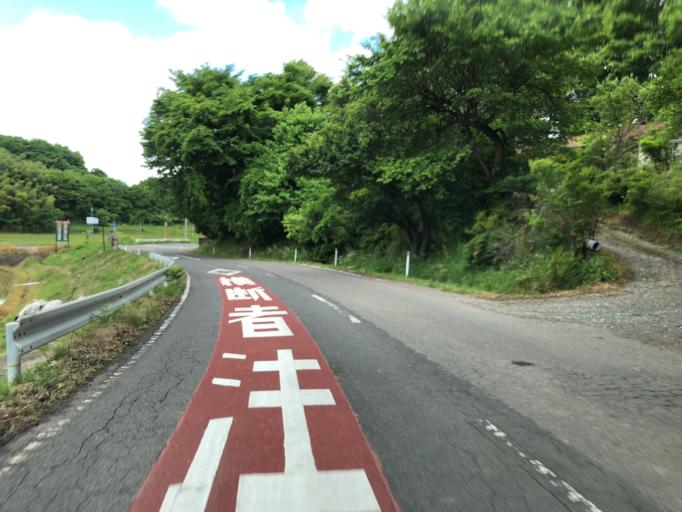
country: JP
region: Fukushima
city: Miharu
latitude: 37.4708
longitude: 140.4613
